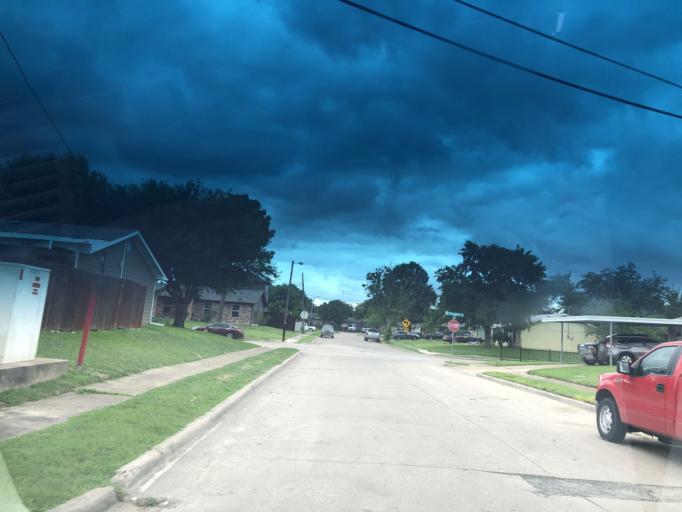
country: US
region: Texas
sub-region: Dallas County
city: Grand Prairie
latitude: 32.7013
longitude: -97.0031
